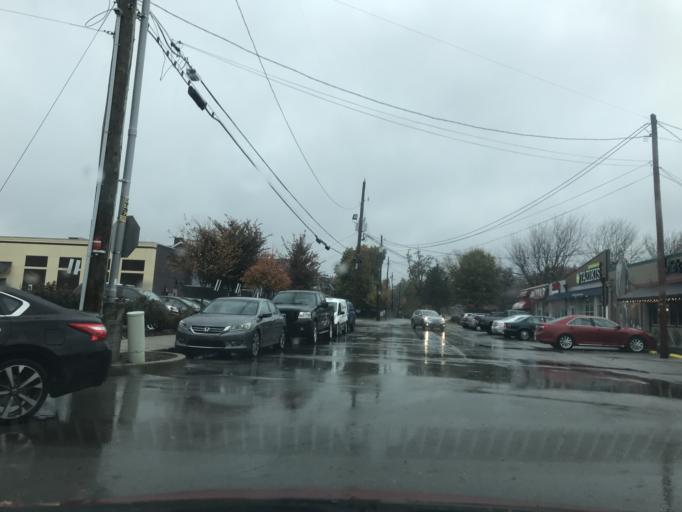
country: US
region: Kentucky
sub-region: Jefferson County
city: Saint Matthews
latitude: 38.2524
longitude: -85.6513
